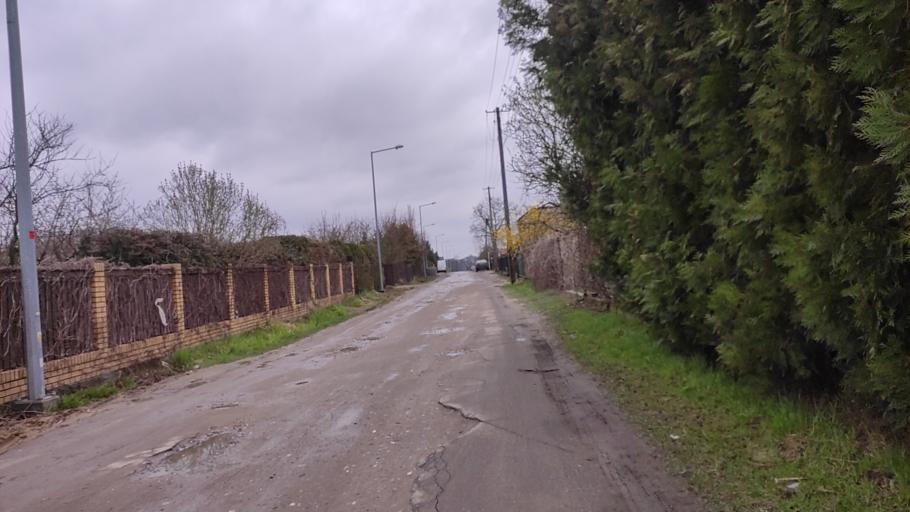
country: PL
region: Greater Poland Voivodeship
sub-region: Powiat poznanski
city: Kostrzyn
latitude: 52.4038
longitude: 17.1644
